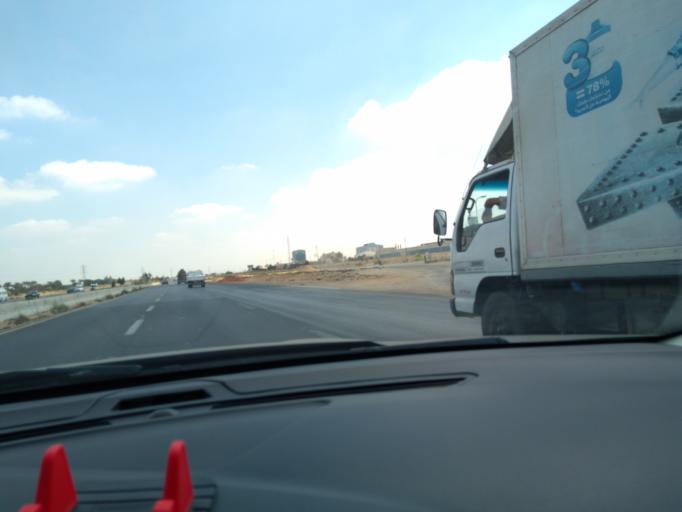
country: EG
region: Al Isma'iliyah
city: At Tall al Kabir
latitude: 30.3386
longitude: 31.8630
